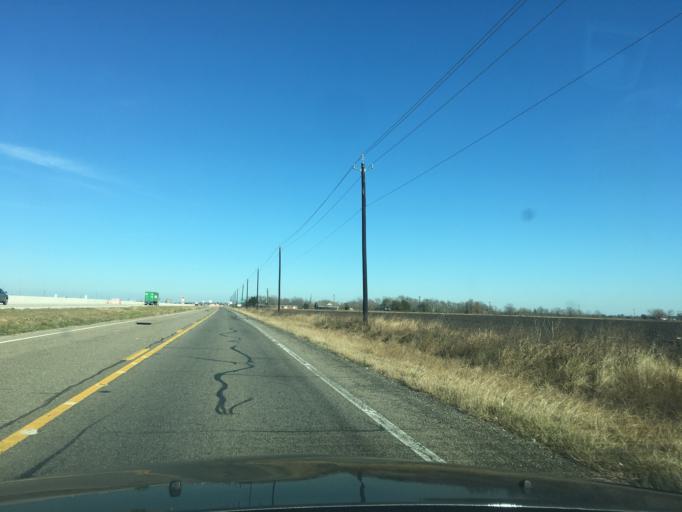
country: US
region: Texas
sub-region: Wharton County
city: East Bernard
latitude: 29.4542
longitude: -95.9853
